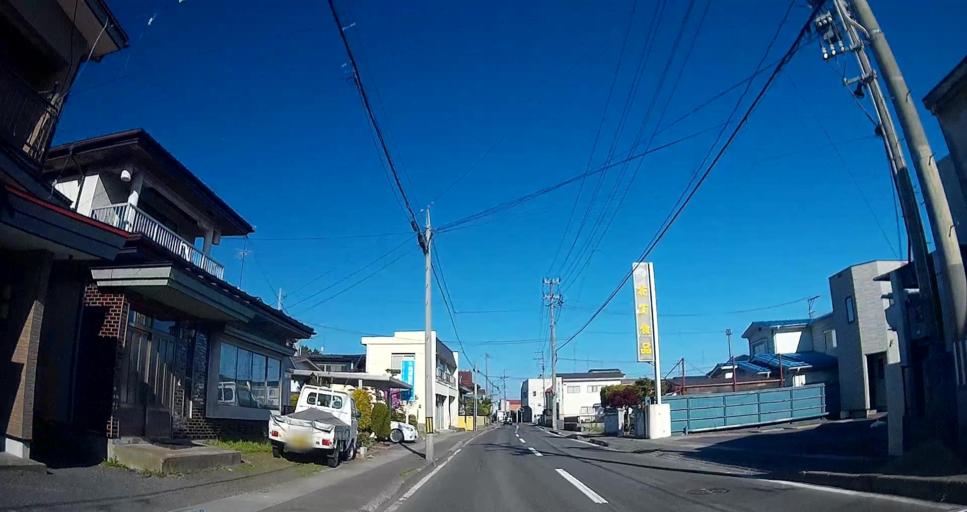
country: JP
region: Aomori
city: Hachinohe
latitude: 40.5231
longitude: 141.5350
